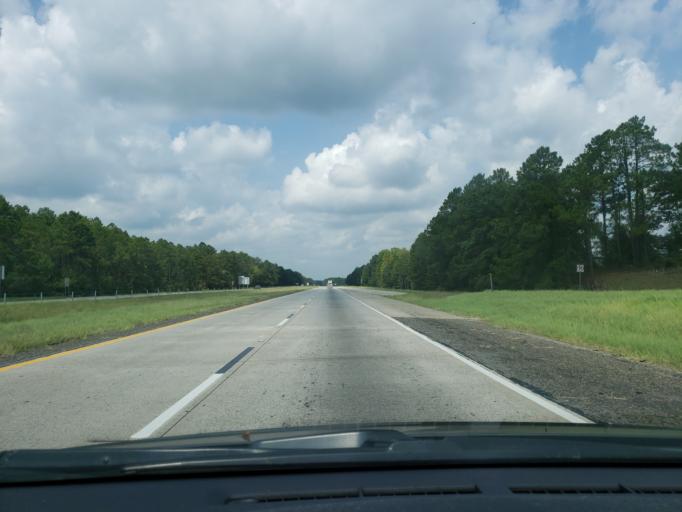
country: US
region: Georgia
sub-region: Treutlen County
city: Soperton
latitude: 32.4342
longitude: -82.6110
